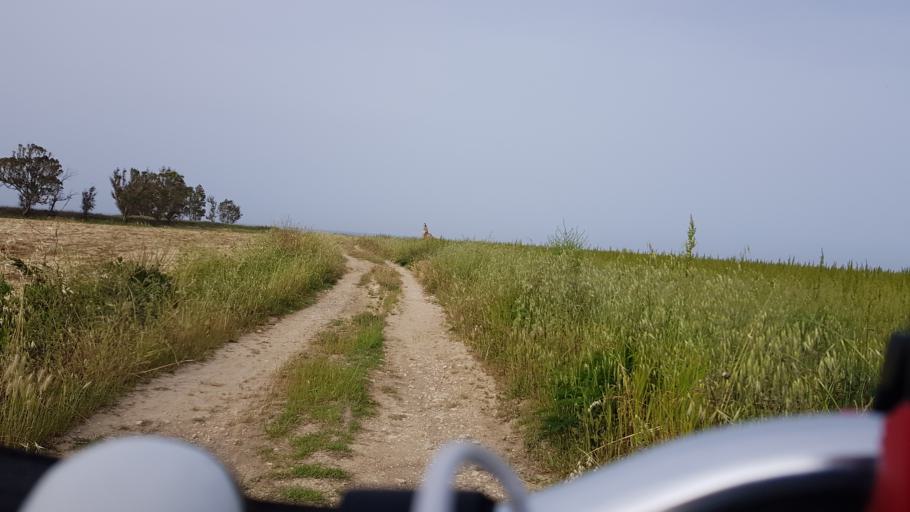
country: IT
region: Apulia
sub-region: Provincia di Brindisi
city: La Rosa
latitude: 40.5804
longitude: 18.0384
